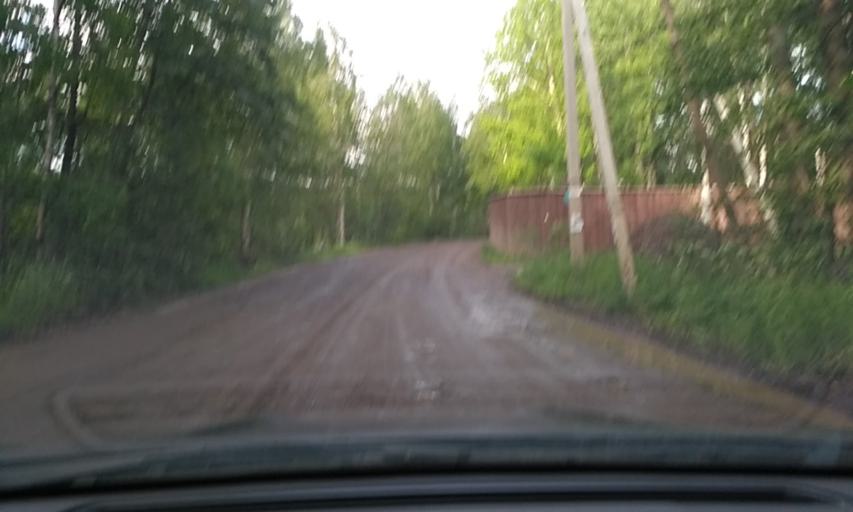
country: RU
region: Leningrad
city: Otradnoye
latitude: 59.7866
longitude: 30.7778
